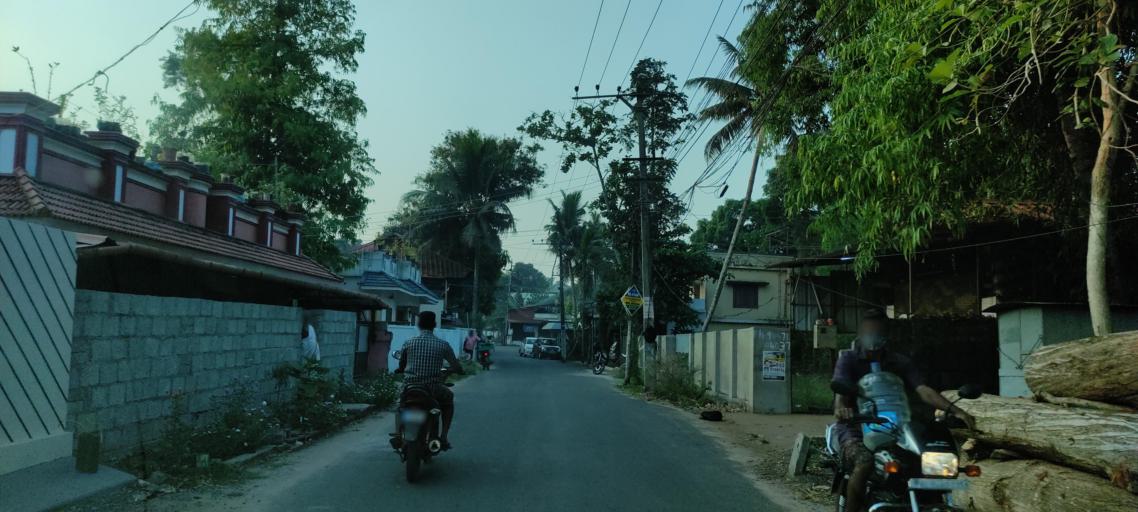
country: IN
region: Kerala
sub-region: Alappuzha
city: Alleppey
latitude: 9.4221
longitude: 76.3484
